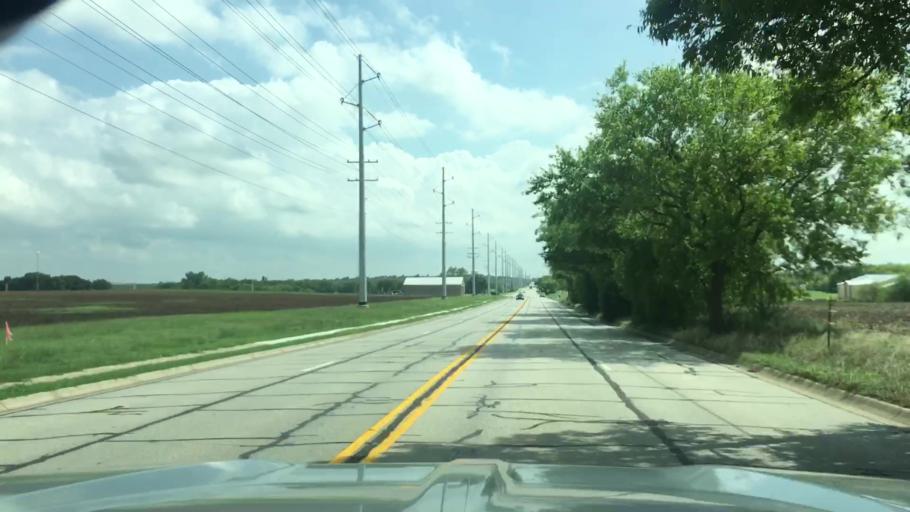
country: US
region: Texas
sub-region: Denton County
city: Denton
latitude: 33.2439
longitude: -97.1607
